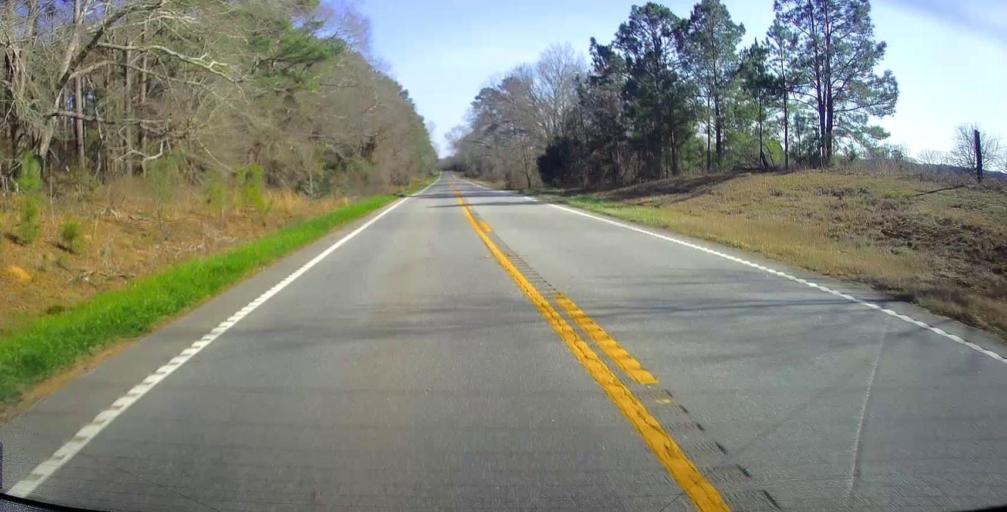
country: US
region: Georgia
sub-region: Macon County
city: Oglethorpe
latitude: 32.3430
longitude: -84.1338
